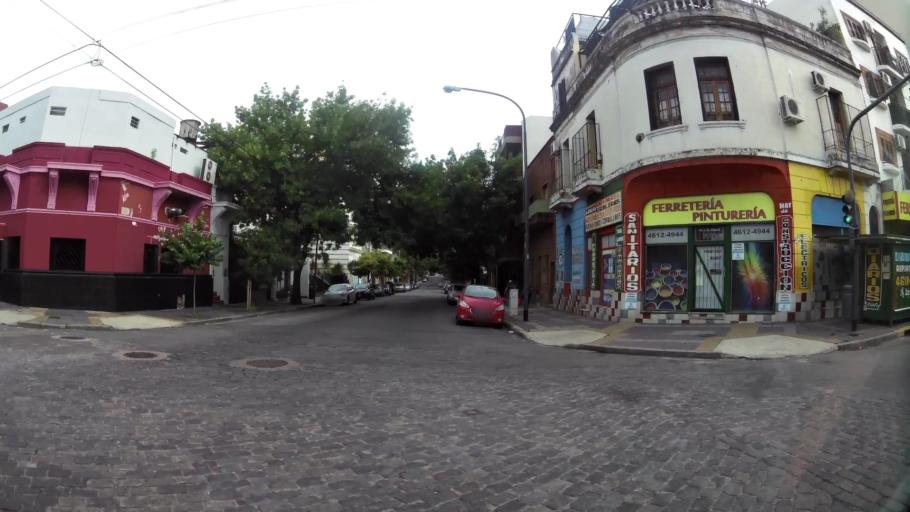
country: AR
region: Buenos Aires F.D.
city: Villa Santa Rita
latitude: -34.6342
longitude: -58.4713
